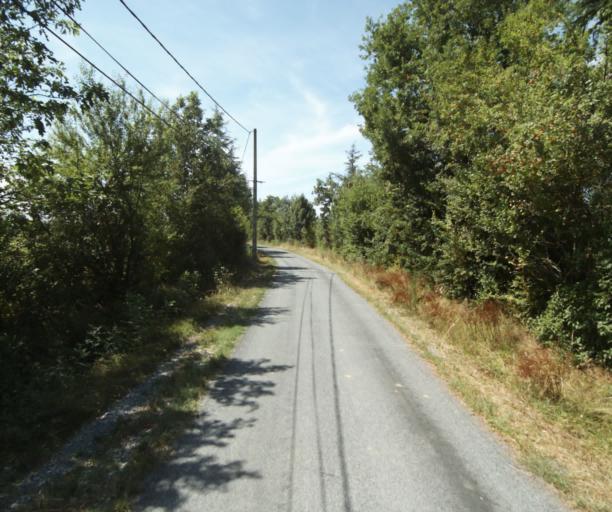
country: FR
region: Midi-Pyrenees
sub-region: Departement du Tarn
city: Puylaurens
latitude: 43.5345
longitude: 2.0047
